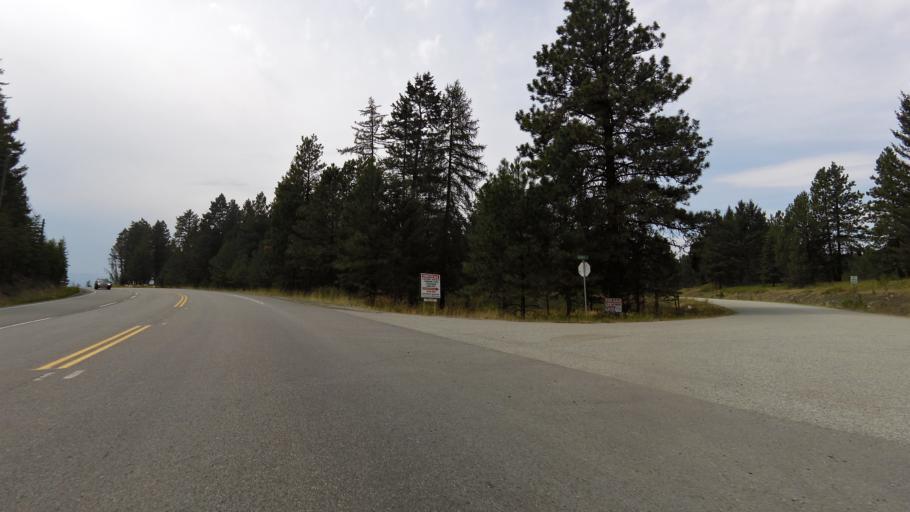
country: CA
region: British Columbia
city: Osoyoos
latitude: 49.0076
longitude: -119.3369
